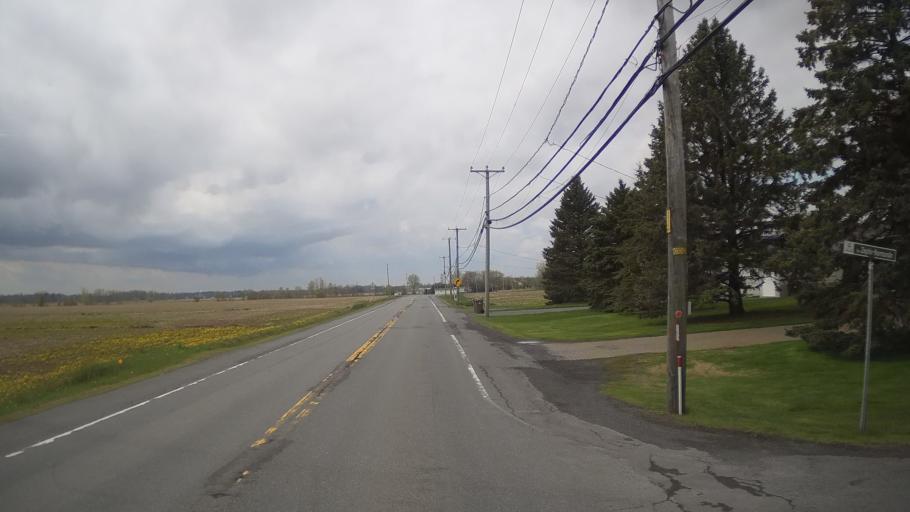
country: CA
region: Quebec
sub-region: Monteregie
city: Saint-Jean-sur-Richelieu
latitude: 45.3316
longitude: -73.1708
